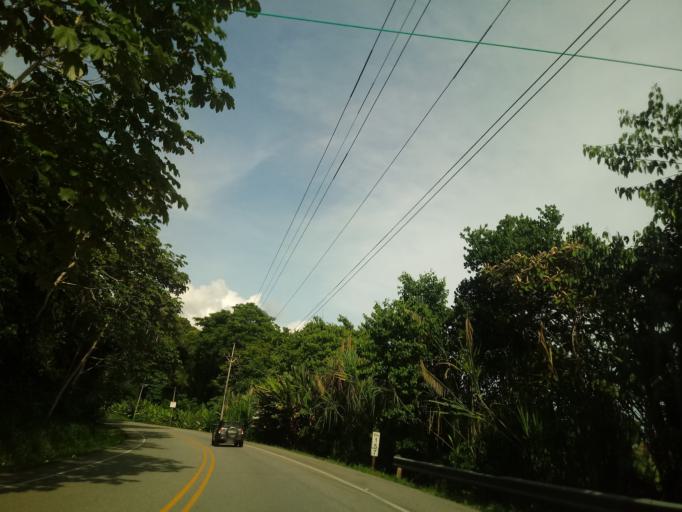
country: CR
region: San Jose
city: Daniel Flores
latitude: 9.1909
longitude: -83.7758
